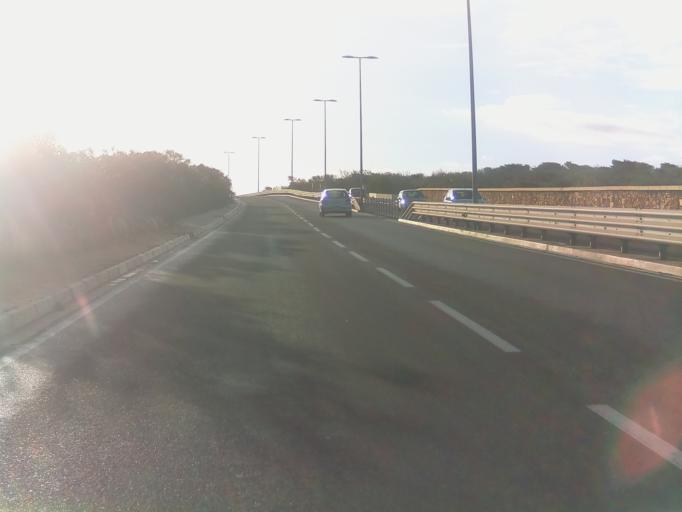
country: MT
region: Il-Mellieha
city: Mellieha
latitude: 35.9808
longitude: 14.3416
